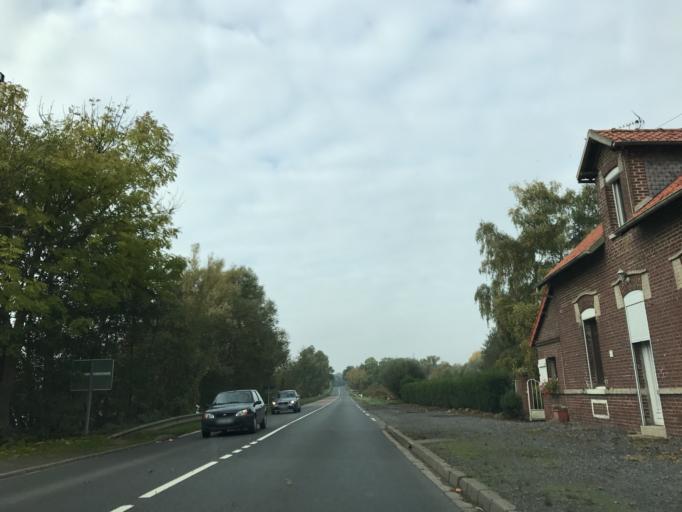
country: FR
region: Picardie
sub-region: Departement de la Somme
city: Peronne
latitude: 49.8765
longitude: 2.9280
